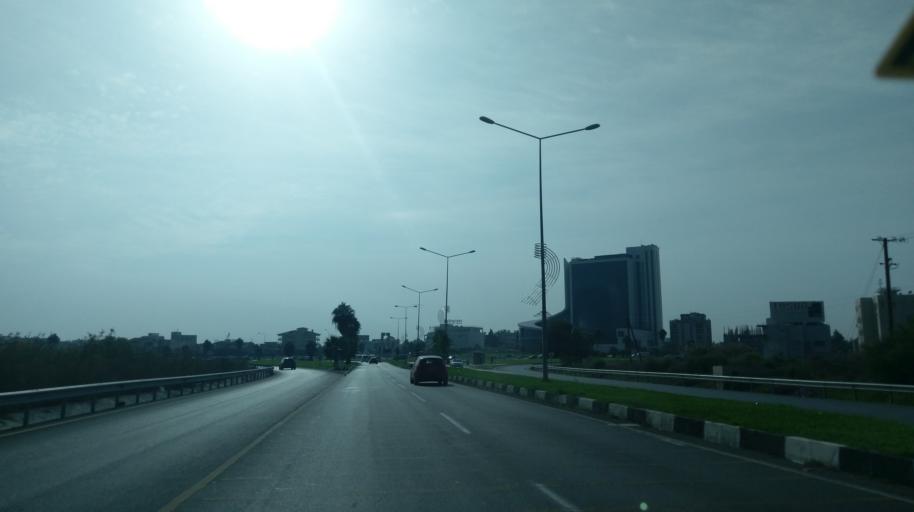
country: CY
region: Lefkosia
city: Nicosia
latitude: 35.2125
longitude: 33.3215
